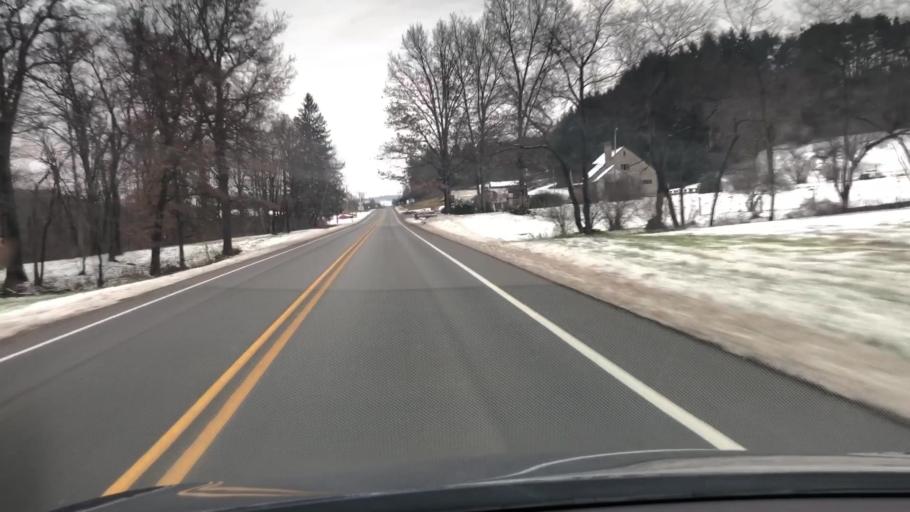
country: US
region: Pennsylvania
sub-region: Jefferson County
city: Brookville
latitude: 41.0820
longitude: -79.2321
